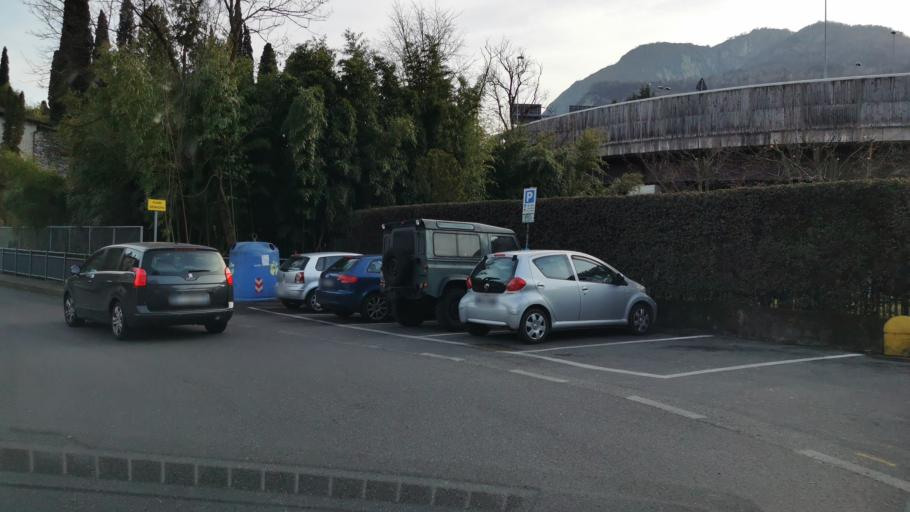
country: IT
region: Lombardy
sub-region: Provincia di Como
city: Menaggio
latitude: 46.0225
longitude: 9.2348
